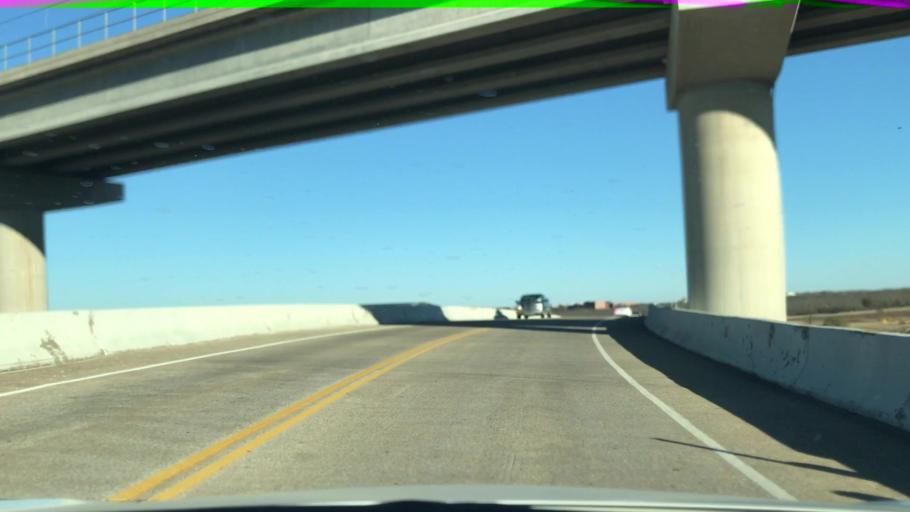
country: US
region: Texas
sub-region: Dallas County
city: Irving
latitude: 32.8805
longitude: -96.9467
